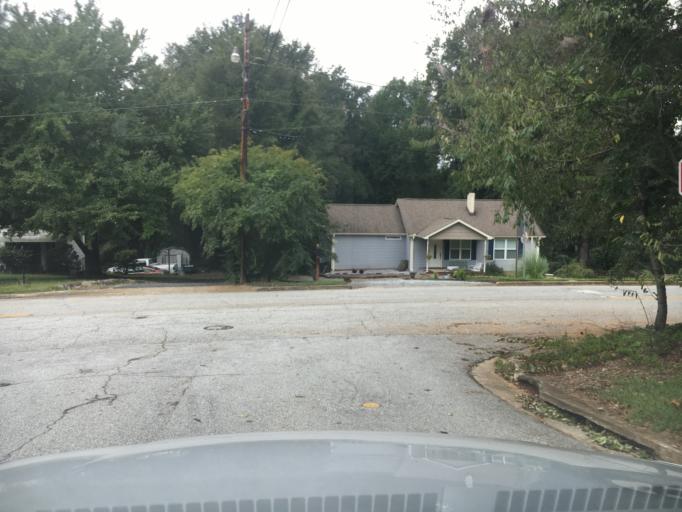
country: US
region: South Carolina
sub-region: Greenville County
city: Greer
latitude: 34.9503
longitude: -82.2294
